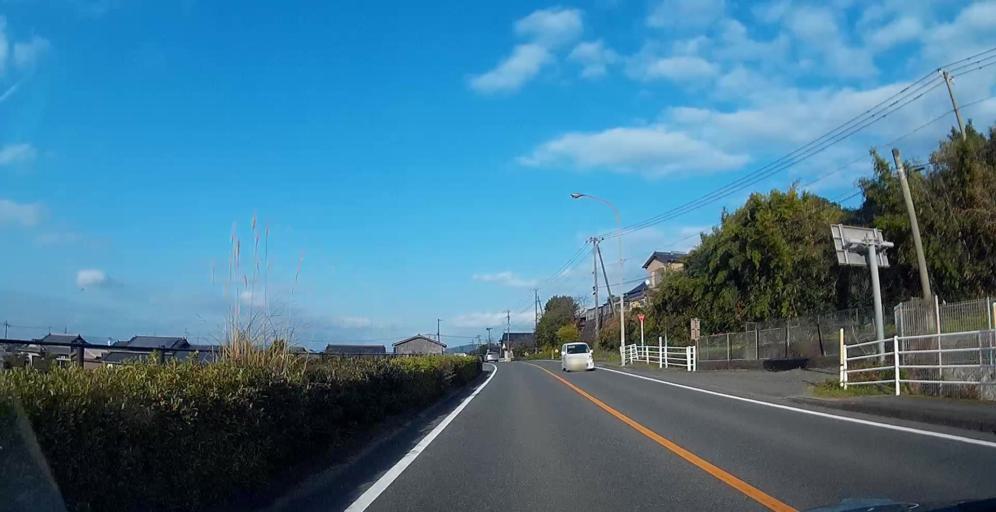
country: JP
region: Kumamoto
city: Matsubase
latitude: 32.5662
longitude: 130.6887
